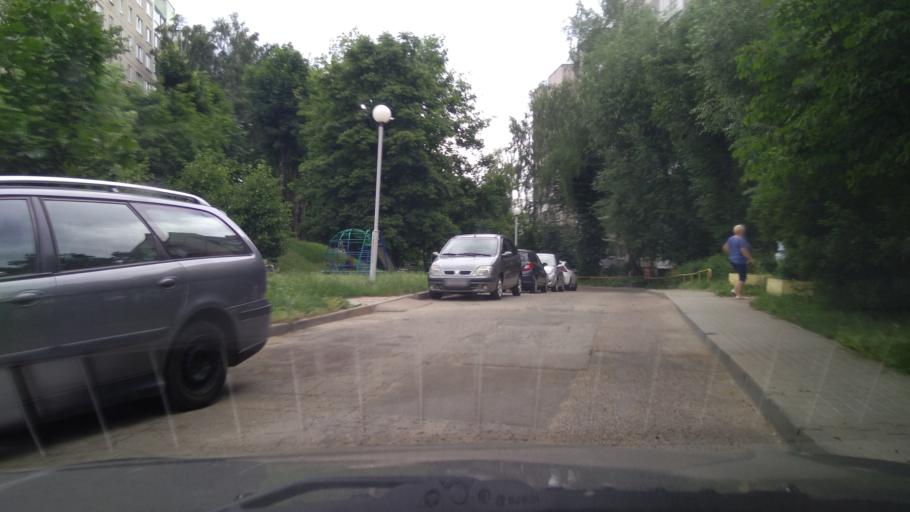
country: BY
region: Minsk
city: Novoye Medvezhino
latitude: 53.8964
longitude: 27.4508
